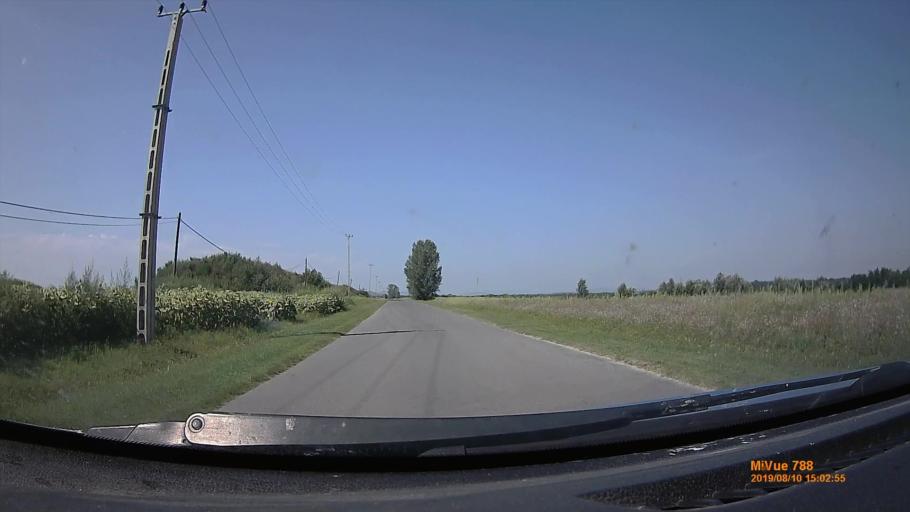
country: HU
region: Somogy
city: Lengyeltoti
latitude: 46.6600
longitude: 17.5735
